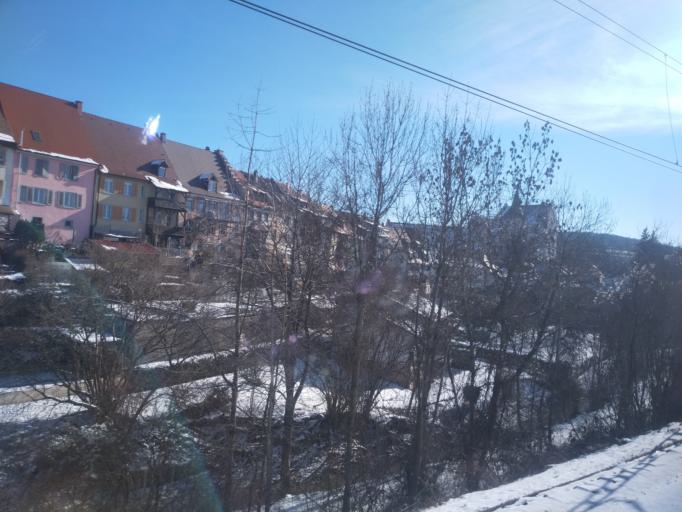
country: DE
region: Baden-Wuerttemberg
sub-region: Freiburg Region
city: Engen
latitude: 47.8513
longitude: 8.7685
